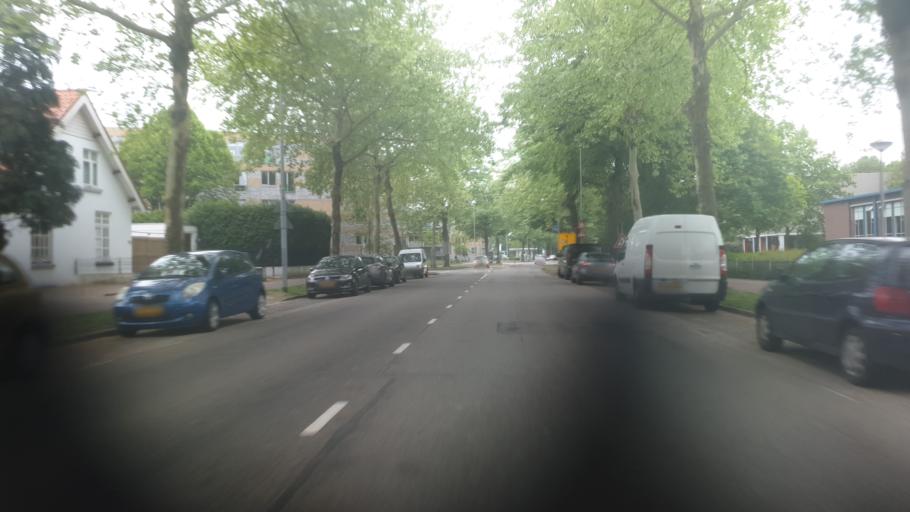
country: NL
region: Gelderland
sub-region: Gemeente Nijmegen
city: Nijmegen
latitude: 51.8155
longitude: 5.8390
